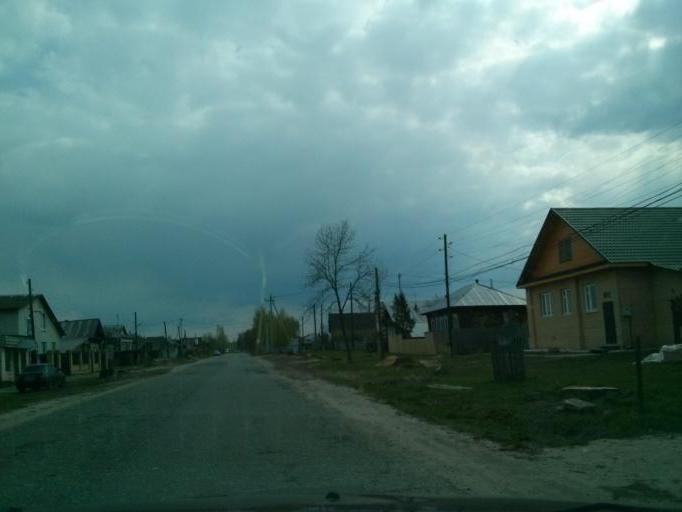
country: RU
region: Nizjnij Novgorod
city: Shimorskoye
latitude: 55.3394
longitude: 41.9287
